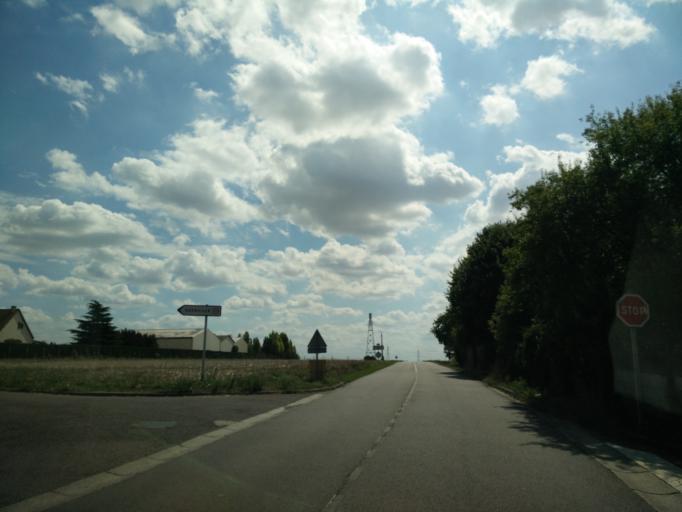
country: FR
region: Ile-de-France
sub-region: Departement des Yvelines
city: Guerville
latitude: 48.9438
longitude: 1.7179
